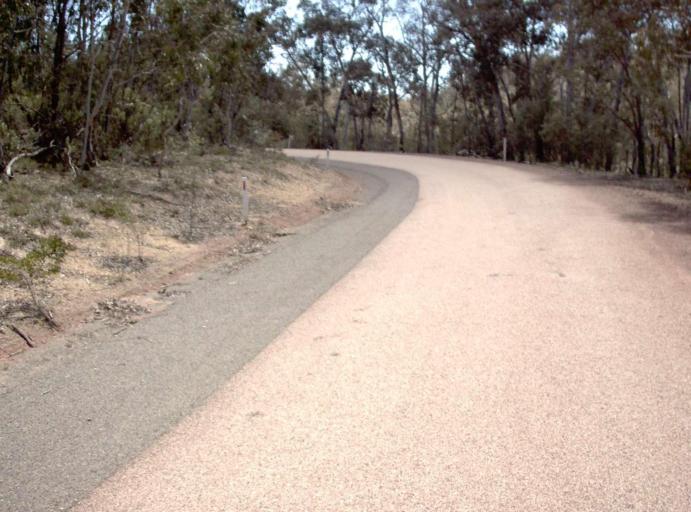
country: AU
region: New South Wales
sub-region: Snowy River
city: Jindabyne
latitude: -37.0690
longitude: 148.2912
